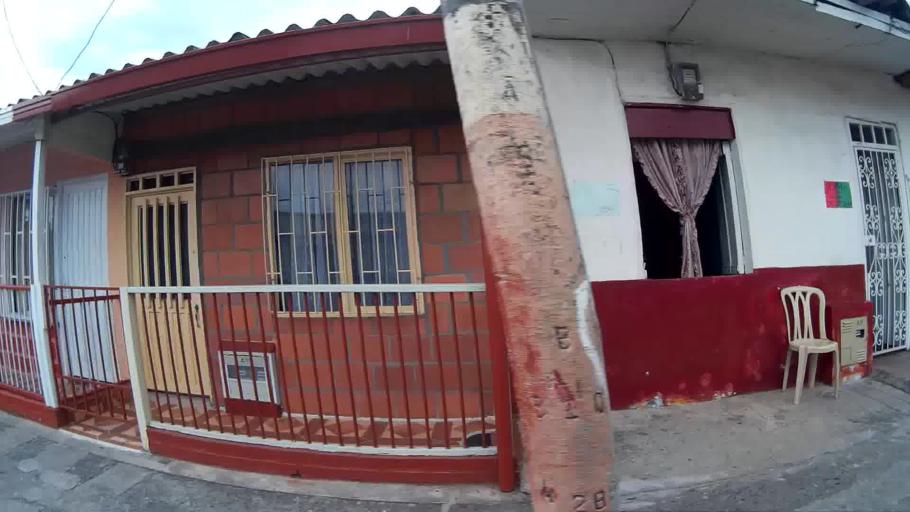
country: CO
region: Valle del Cauca
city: Ulloa
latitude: 4.7377
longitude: -75.7127
